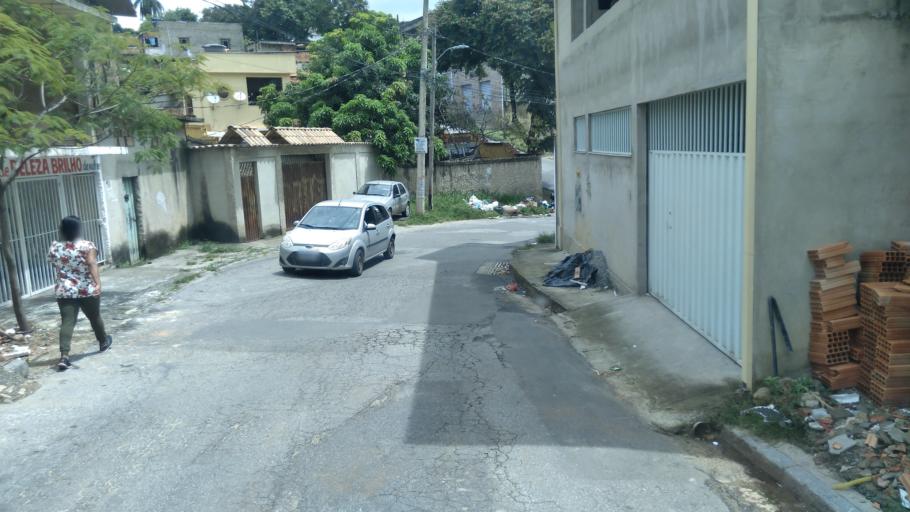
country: BR
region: Minas Gerais
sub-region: Belo Horizonte
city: Belo Horizonte
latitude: -19.8509
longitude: -43.8935
